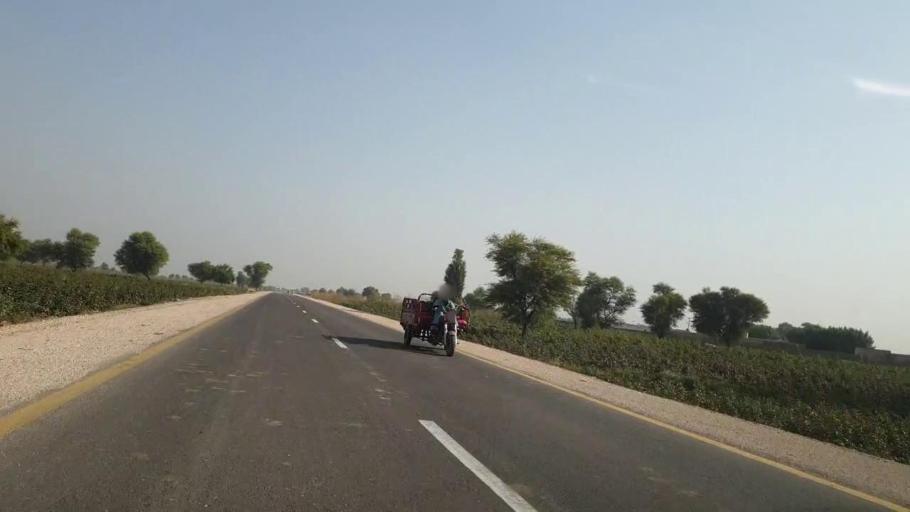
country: PK
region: Sindh
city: Sehwan
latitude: 26.4682
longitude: 67.7948
